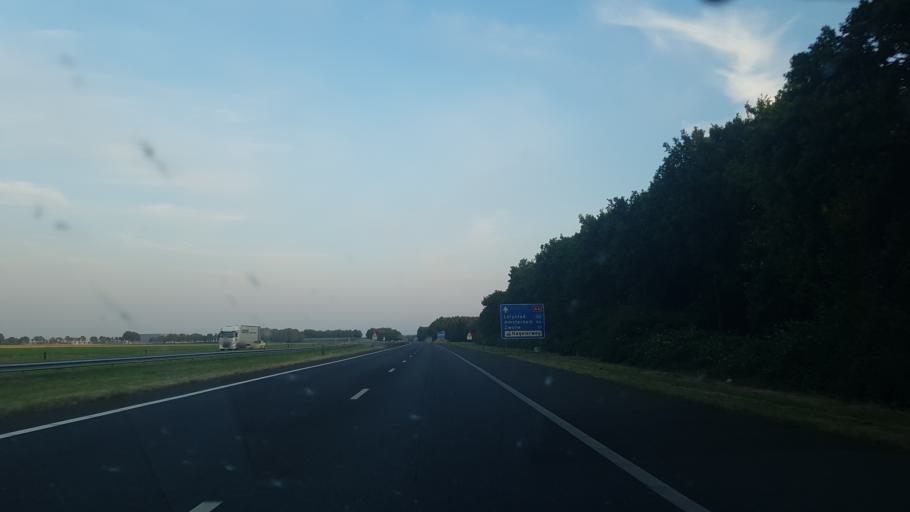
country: NL
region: Flevoland
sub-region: Gemeente Noordoostpolder
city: Emmeloord
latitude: 52.7363
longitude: 5.7689
